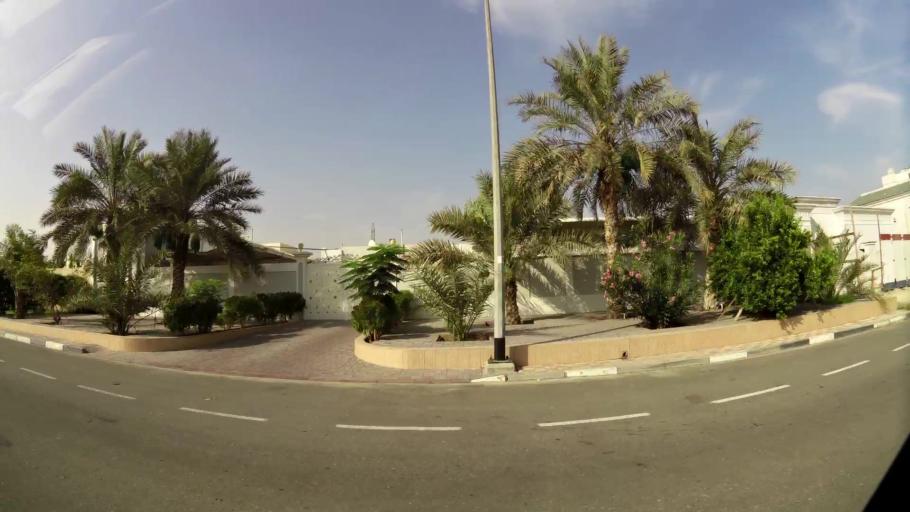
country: AE
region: Ash Shariqah
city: Sharjah
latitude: 25.2162
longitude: 55.3859
